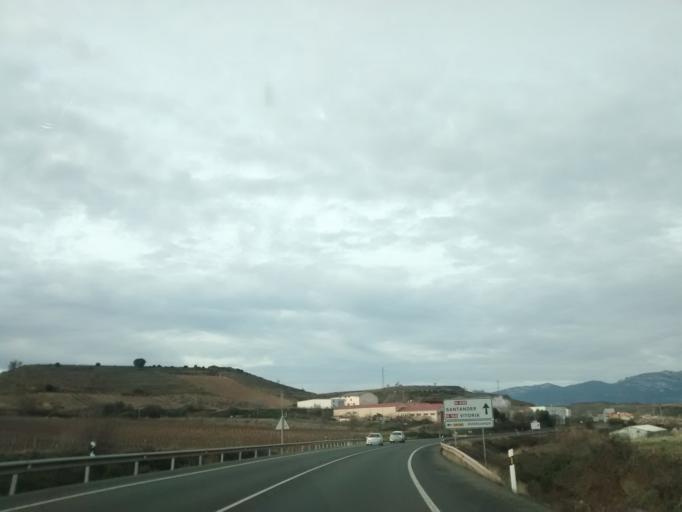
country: ES
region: La Rioja
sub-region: Provincia de La Rioja
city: Cenicero
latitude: 42.4730
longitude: -2.6422
